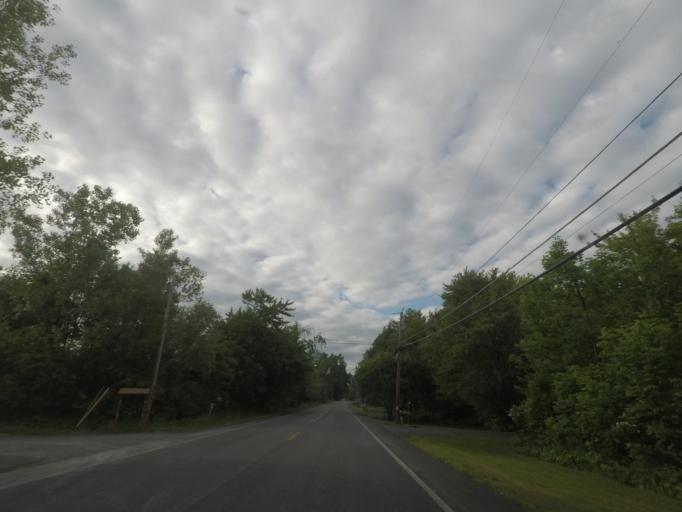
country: US
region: New York
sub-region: Ulster County
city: Plattekill
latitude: 41.5960
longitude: -74.1178
